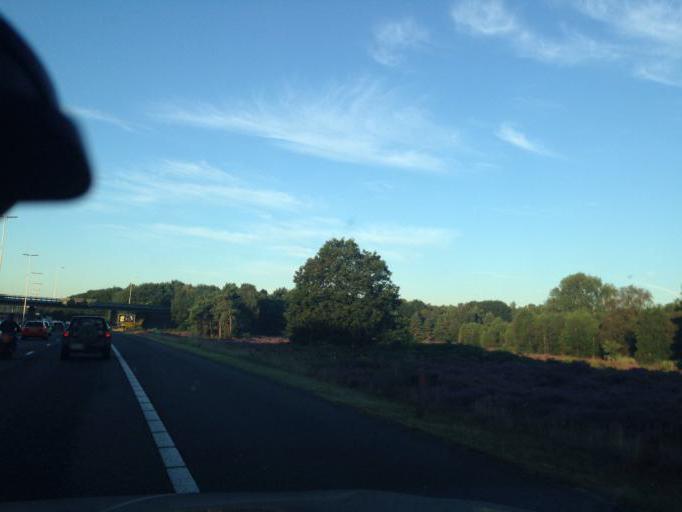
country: NL
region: North Holland
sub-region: Gemeente Hilversum
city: Hilversum
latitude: 52.2044
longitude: 5.1964
